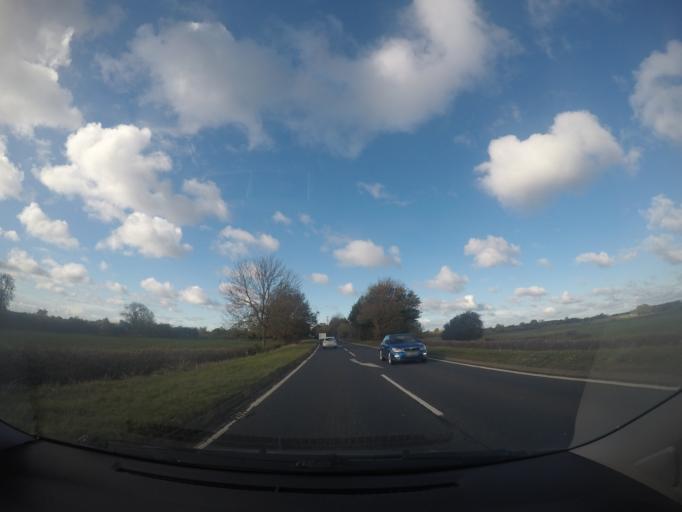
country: GB
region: England
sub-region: City and Borough of Leeds
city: Walton
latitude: 53.9981
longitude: -1.2621
